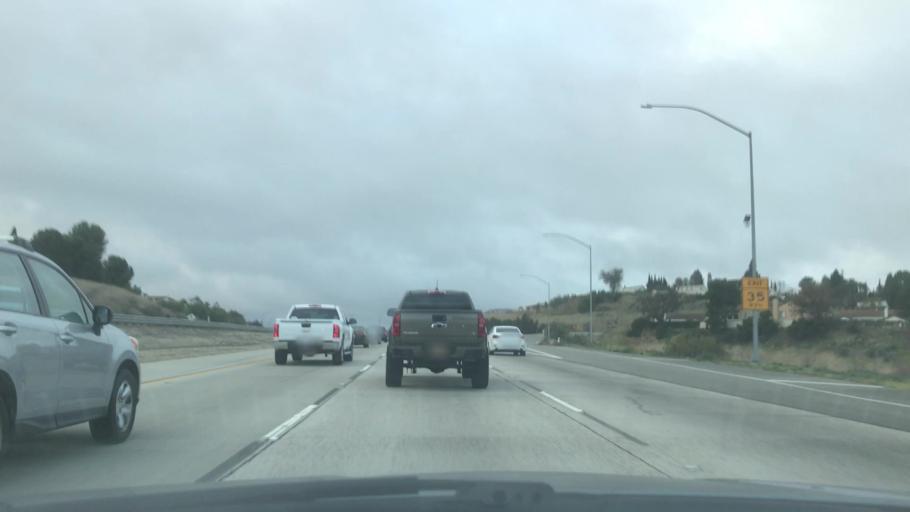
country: US
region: California
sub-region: Ventura County
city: Thousand Oaks
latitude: 34.2314
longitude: -118.8452
